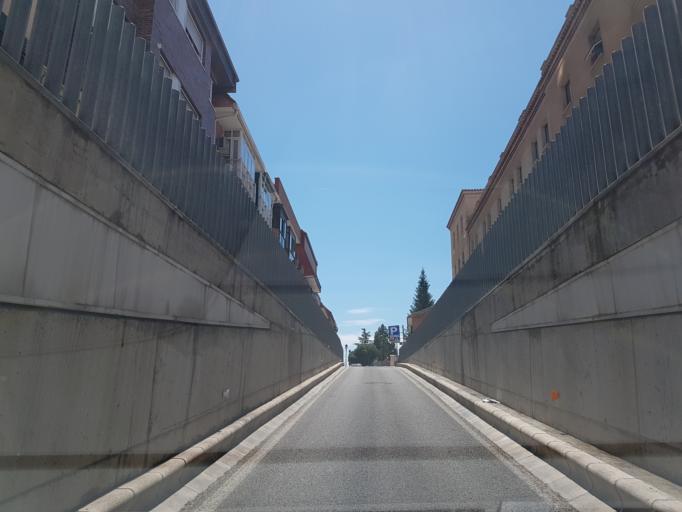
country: ES
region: Madrid
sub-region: Provincia de Madrid
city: Pozuelo de Alarcon
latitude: 40.4347
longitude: -3.8139
